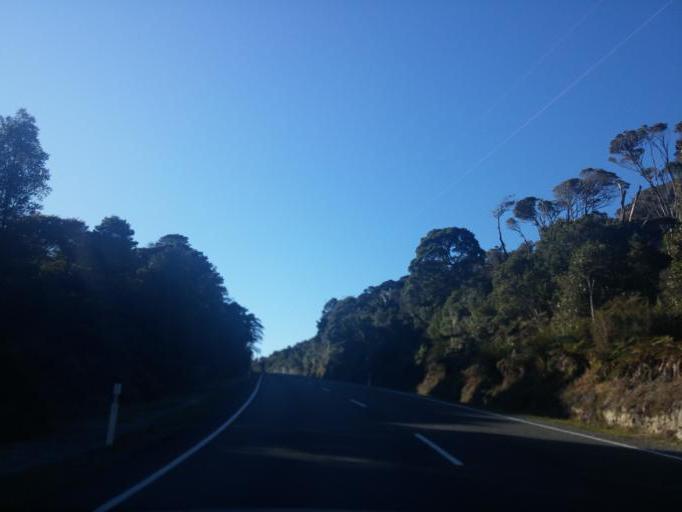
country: NZ
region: West Coast
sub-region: Grey District
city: Greymouth
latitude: -42.0973
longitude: 171.3429
